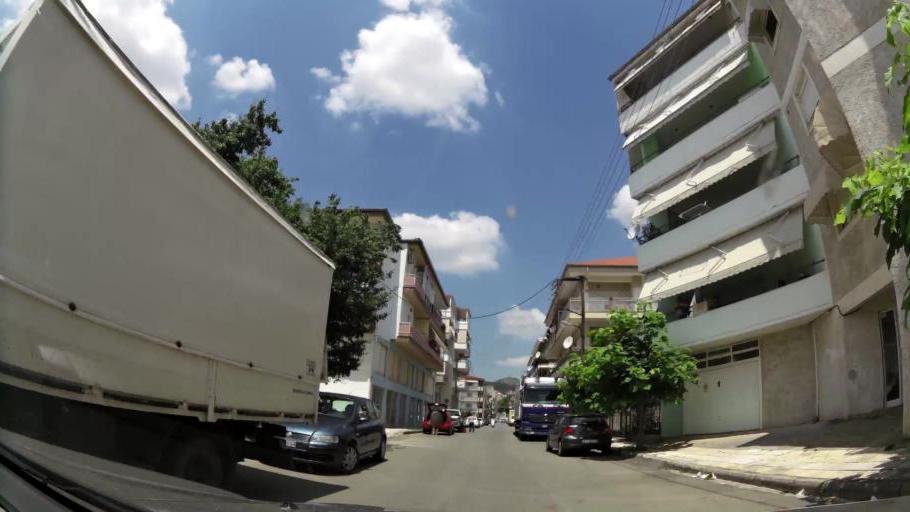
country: GR
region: West Macedonia
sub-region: Nomos Kozanis
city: Kozani
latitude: 40.2955
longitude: 21.7936
